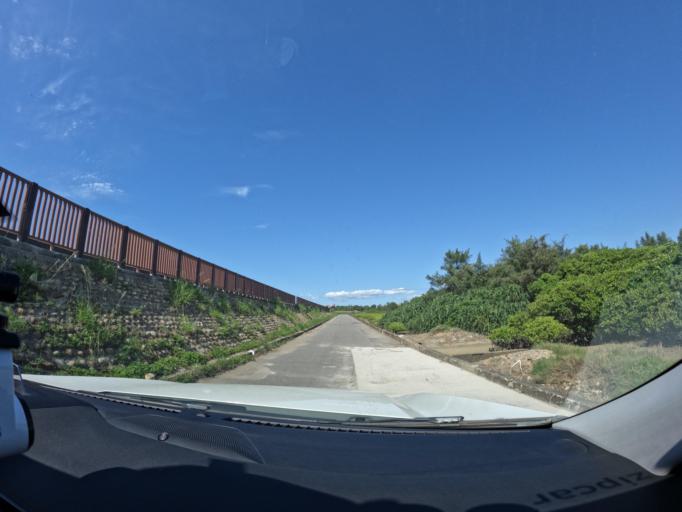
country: TW
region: Taiwan
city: Taoyuan City
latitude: 25.0944
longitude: 121.1917
